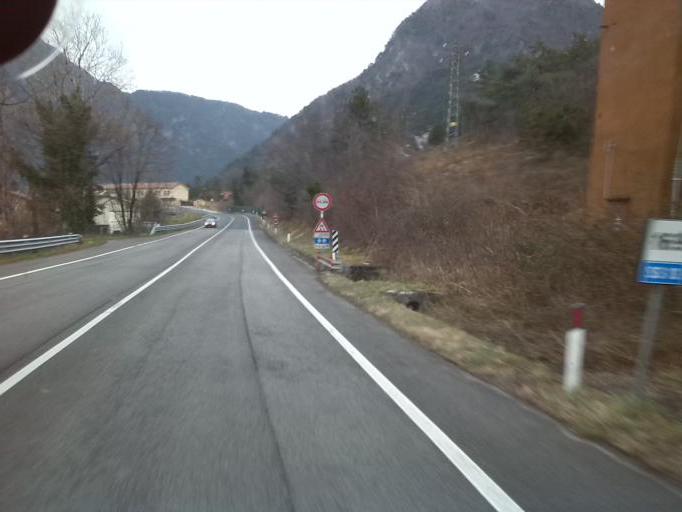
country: IT
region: Friuli Venezia Giulia
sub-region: Provincia di Udine
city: Amaro
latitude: 46.3743
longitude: 13.1363
